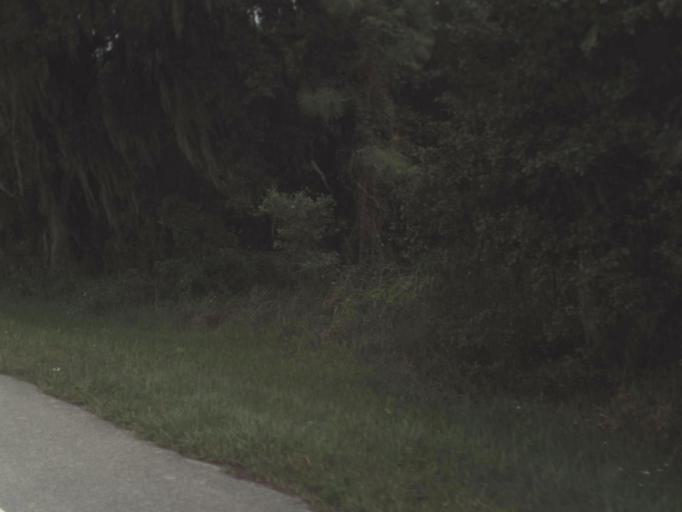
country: US
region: Florida
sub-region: Hardee County
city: Bowling Green
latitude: 27.5948
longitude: -81.8866
